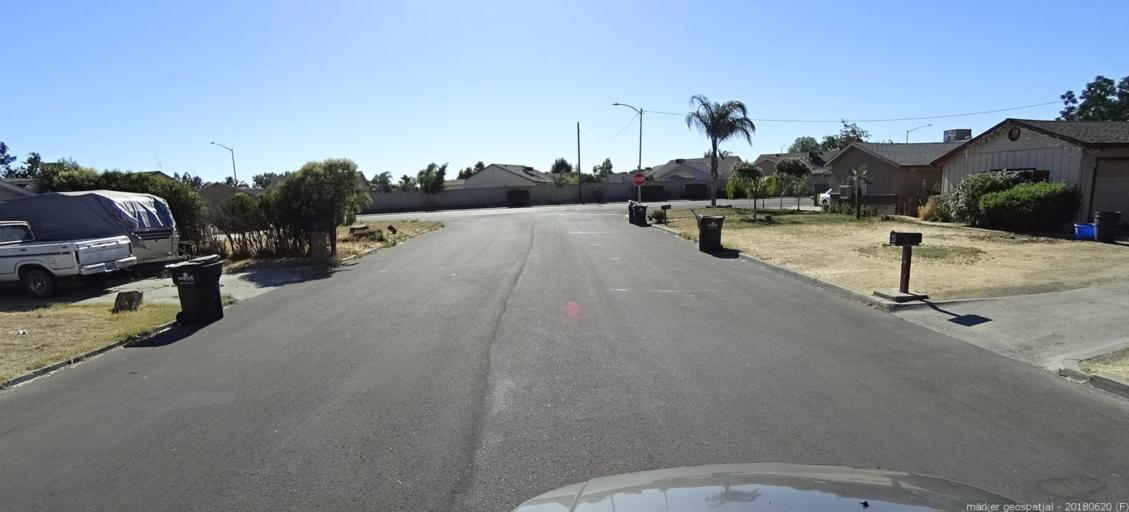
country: US
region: California
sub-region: Madera County
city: Parkwood
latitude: 36.9373
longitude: -120.0488
